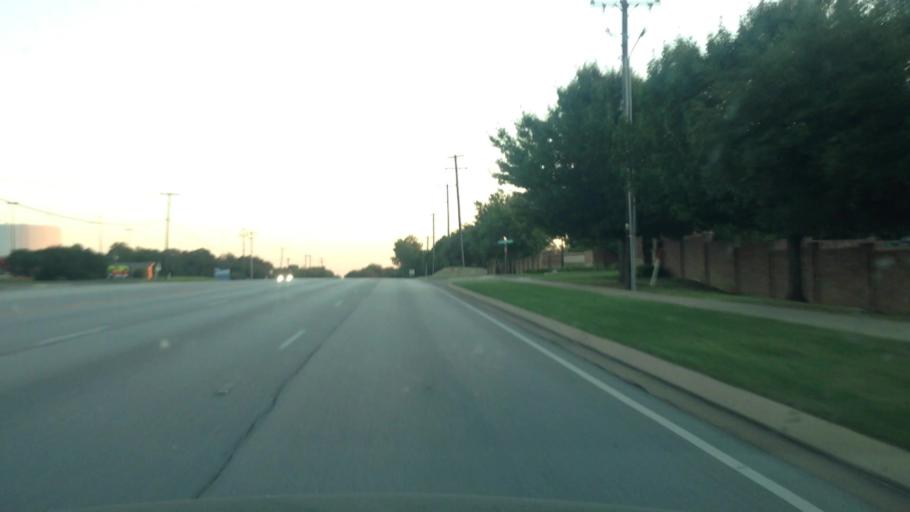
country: US
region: Texas
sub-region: Tarrant County
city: North Richland Hills
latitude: 32.8544
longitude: -97.2127
